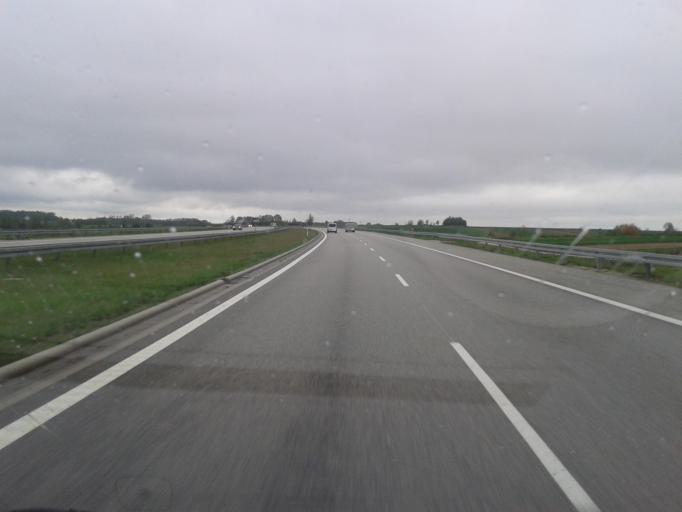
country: PL
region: Subcarpathian Voivodeship
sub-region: Powiat debicki
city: Czarna
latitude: 50.0973
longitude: 21.2888
